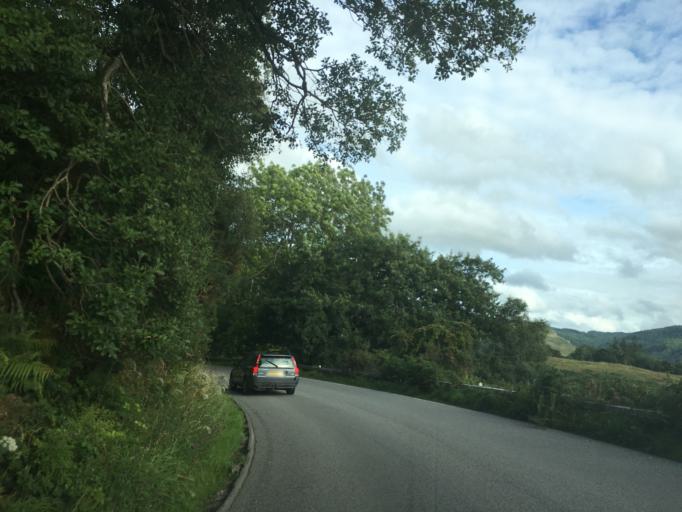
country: GB
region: Scotland
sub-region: Argyll and Bute
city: Oban
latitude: 56.3772
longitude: -5.4575
